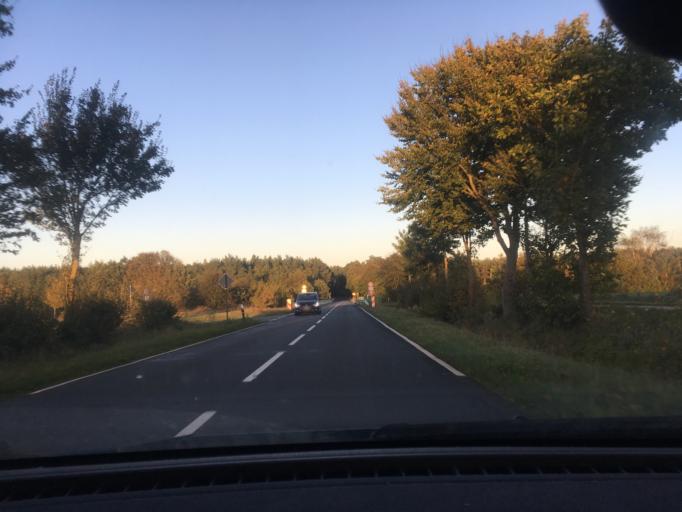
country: DE
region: Lower Saxony
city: Wendisch Evern
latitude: 53.2211
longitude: 10.4900
